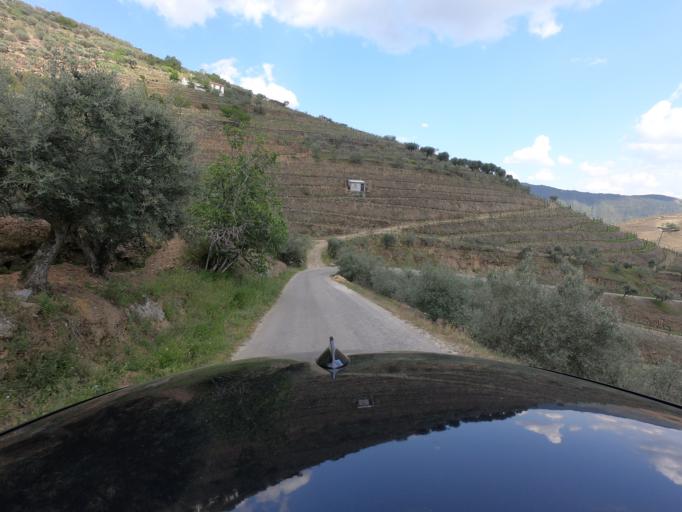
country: PT
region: Vila Real
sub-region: Sabrosa
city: Vilela
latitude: 41.2012
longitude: -7.6618
